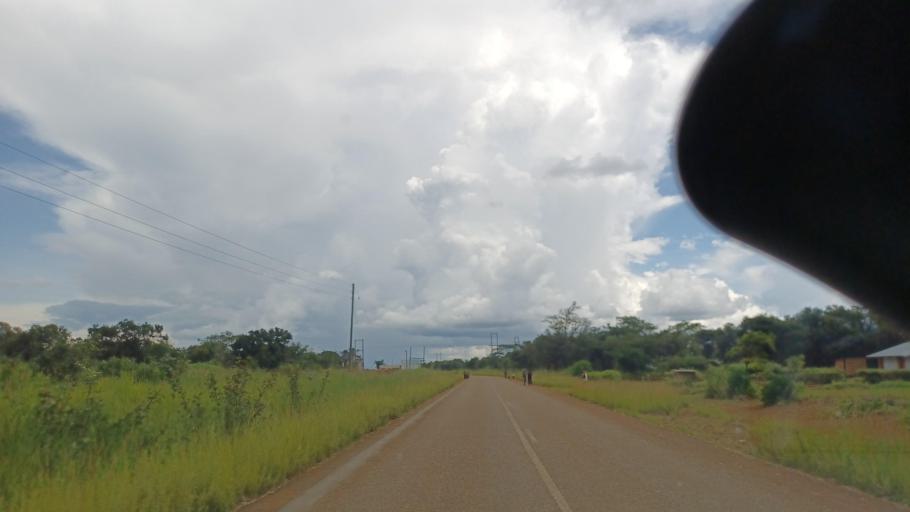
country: ZM
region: North-Western
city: Kasempa
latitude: -13.1111
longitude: 25.8698
